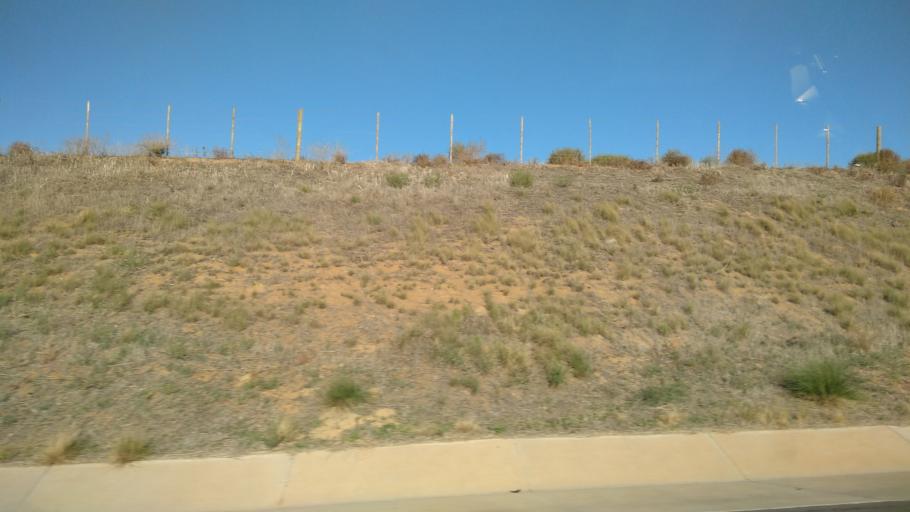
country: ZA
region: Western Cape
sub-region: West Coast District Municipality
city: Malmesbury
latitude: -33.4249
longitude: 18.7177
